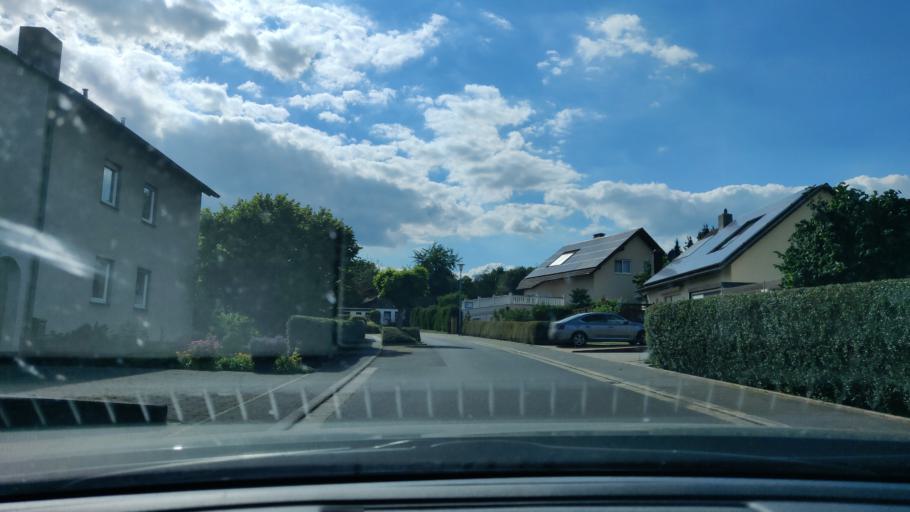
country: DE
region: Hesse
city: Fritzlar
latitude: 51.1379
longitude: 9.2830
